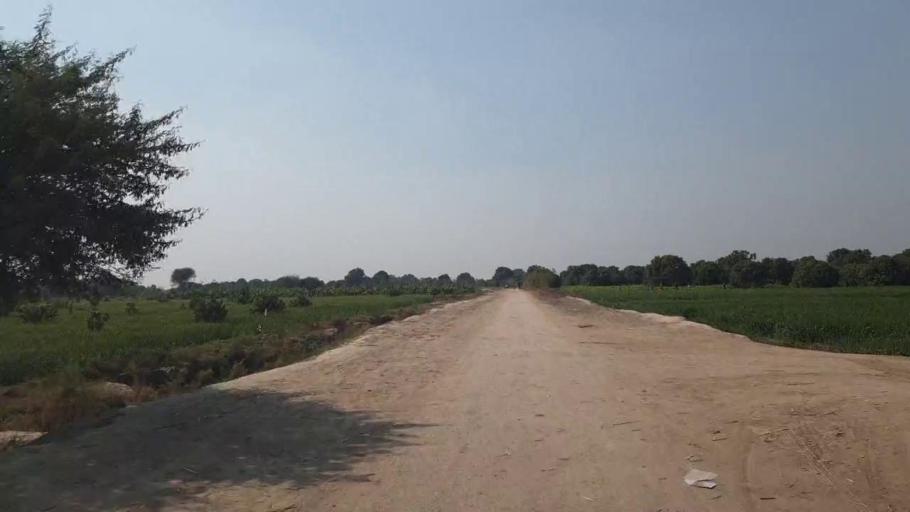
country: PK
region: Sindh
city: Chambar
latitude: 25.3768
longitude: 68.8779
